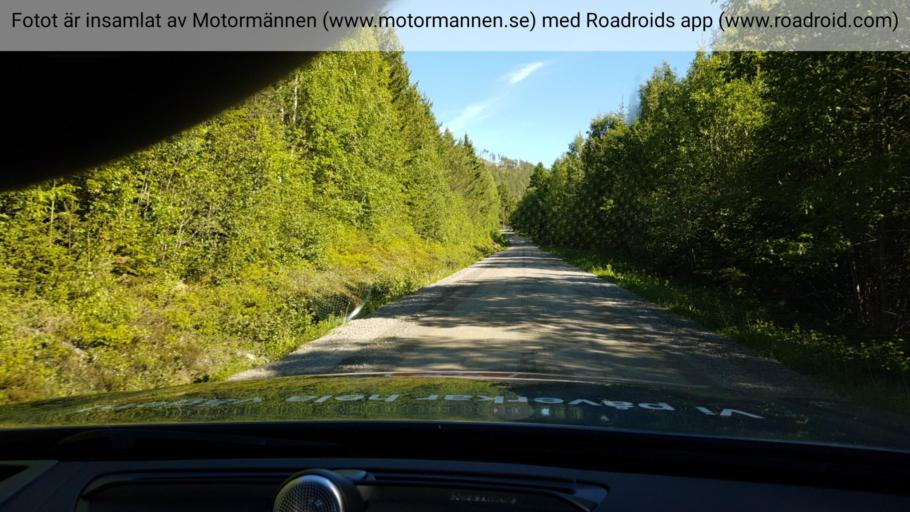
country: SE
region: Jaemtland
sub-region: Bergs Kommun
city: Hoverberg
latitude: 62.7092
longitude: 14.7065
